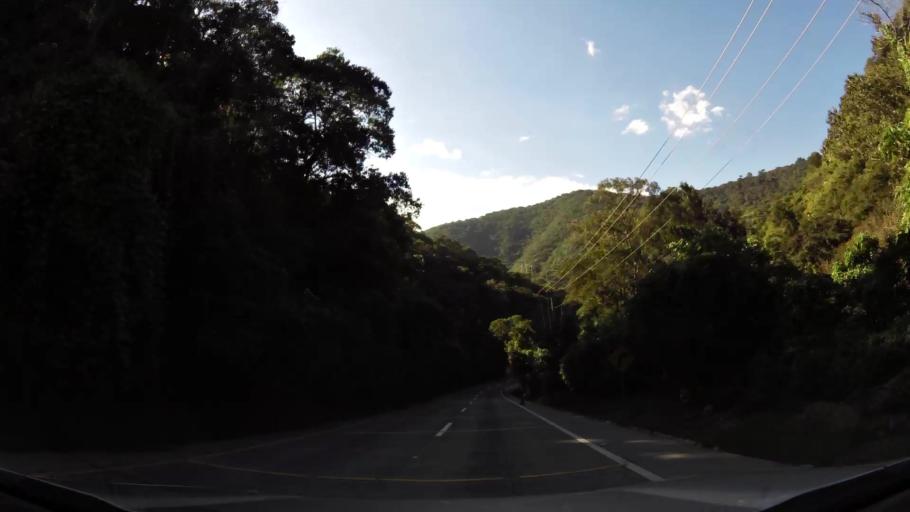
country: GT
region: Sacatepequez
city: Santa Lucia Milpas Altas
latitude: 14.5656
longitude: -90.6970
